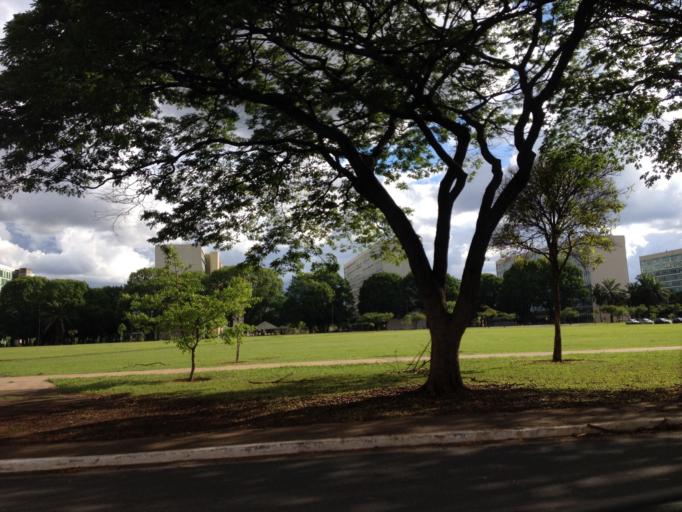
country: BR
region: Federal District
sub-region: Brasilia
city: Brasilia
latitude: -15.7968
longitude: -47.8700
